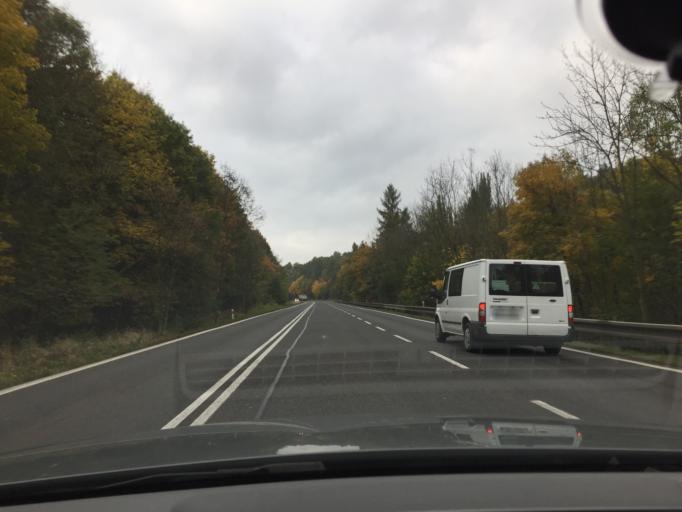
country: CZ
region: Ustecky
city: Velemin
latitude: 50.5598
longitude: 13.9631
